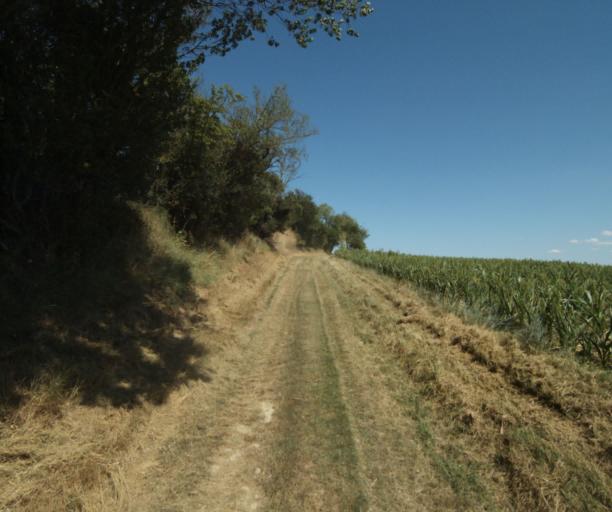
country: FR
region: Midi-Pyrenees
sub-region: Departement de la Haute-Garonne
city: Saint-Felix-Lauragais
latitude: 43.4881
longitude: 1.8971
